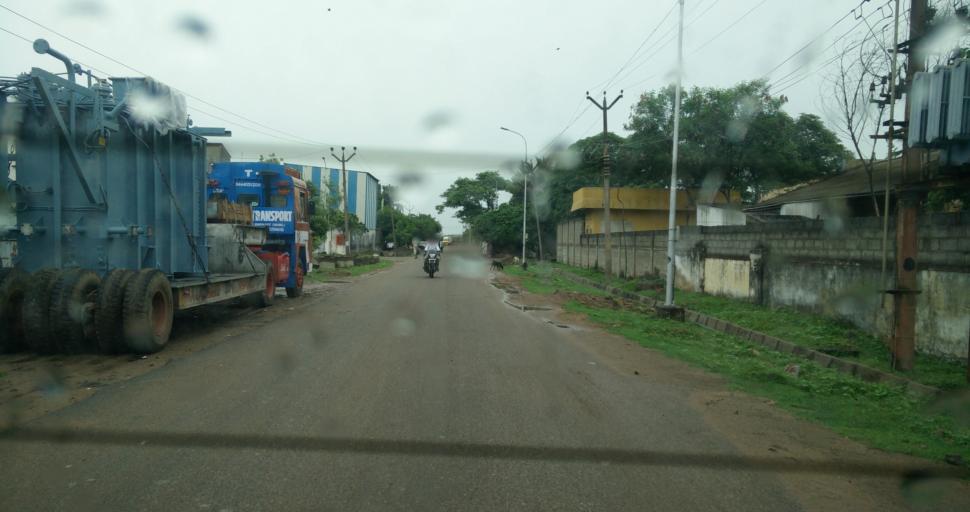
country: IN
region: Tamil Nadu
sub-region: Kancheepuram
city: Poonamalle
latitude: 13.0468
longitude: 80.0566
